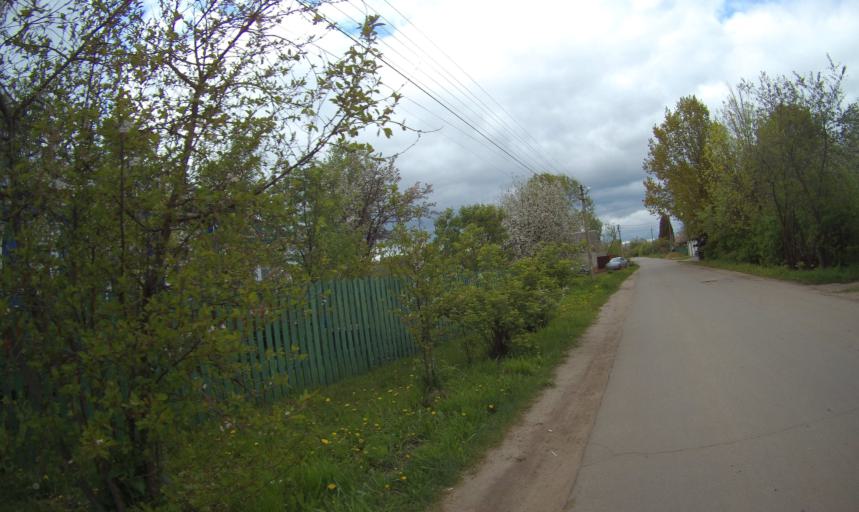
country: RU
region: Moskovskaya
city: Rechitsy
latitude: 55.5806
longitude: 38.5047
